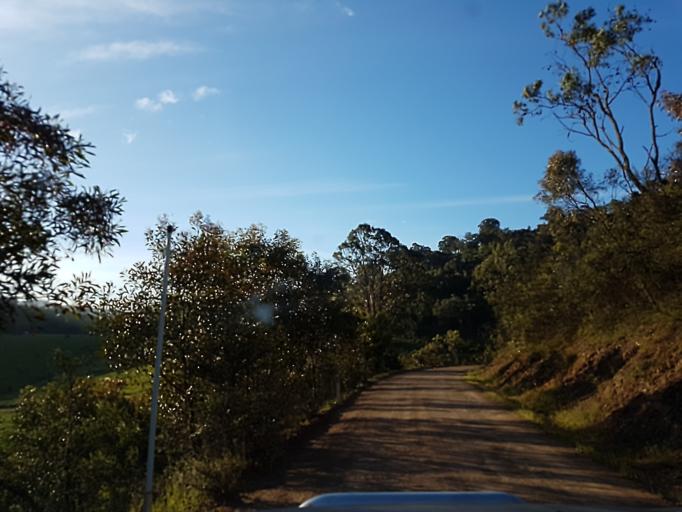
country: AU
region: Victoria
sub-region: East Gippsland
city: Bairnsdale
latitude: -37.4133
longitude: 147.1239
